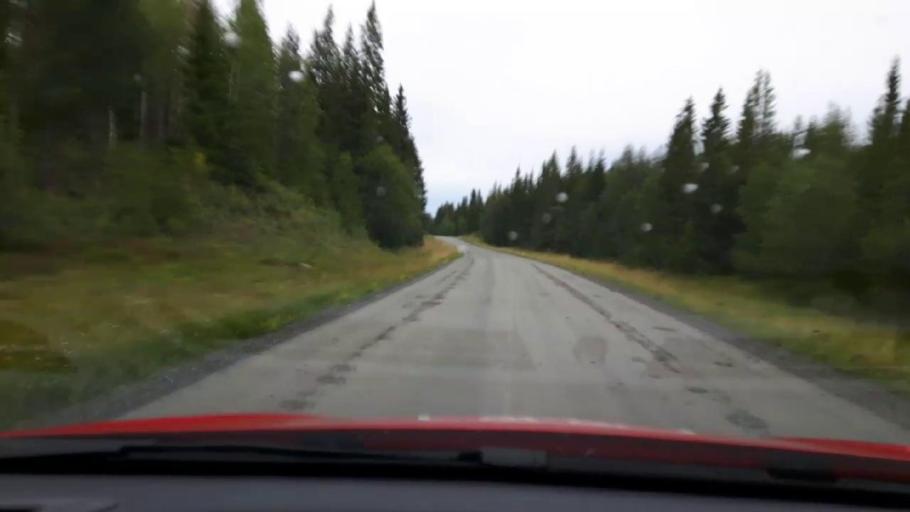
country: SE
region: Jaemtland
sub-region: Are Kommun
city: Are
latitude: 63.4332
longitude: 13.2751
